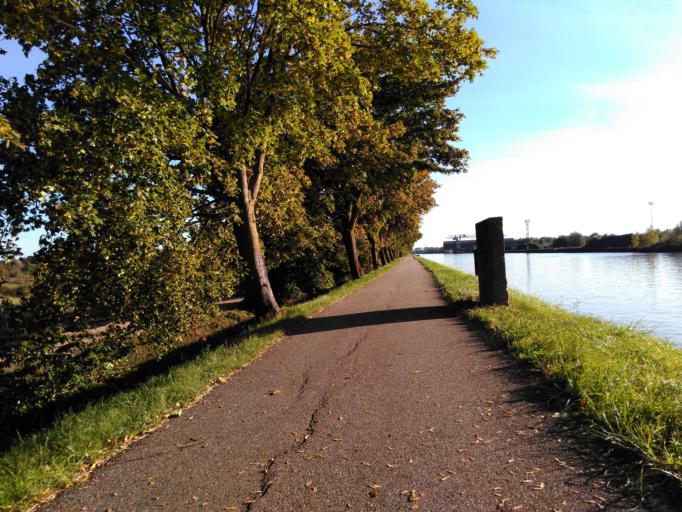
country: FR
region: Lorraine
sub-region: Departement de la Moselle
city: Bousse
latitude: 49.2771
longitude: 6.1822
